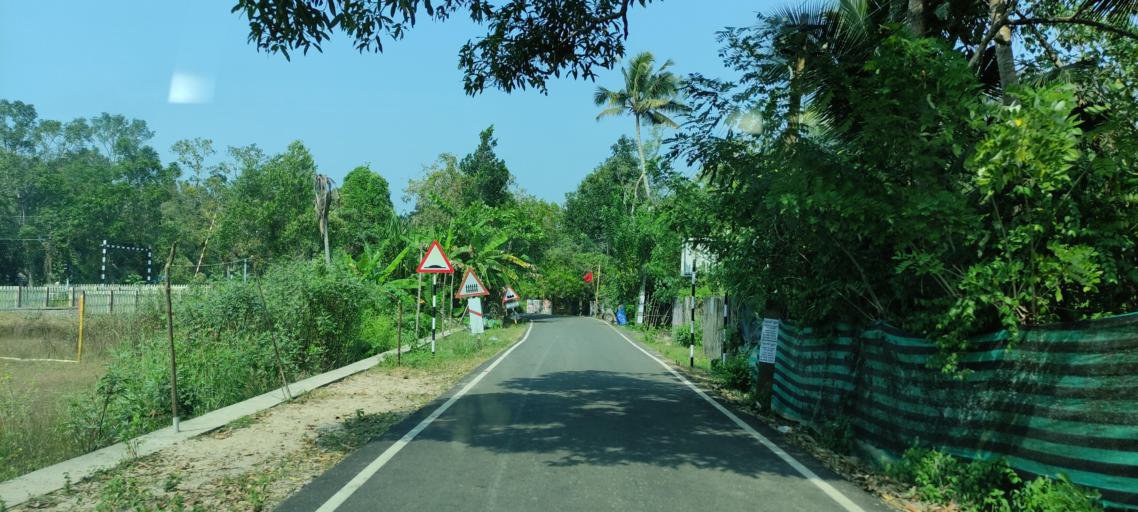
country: IN
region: Kerala
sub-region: Alappuzha
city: Alleppey
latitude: 9.5530
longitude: 76.3194
